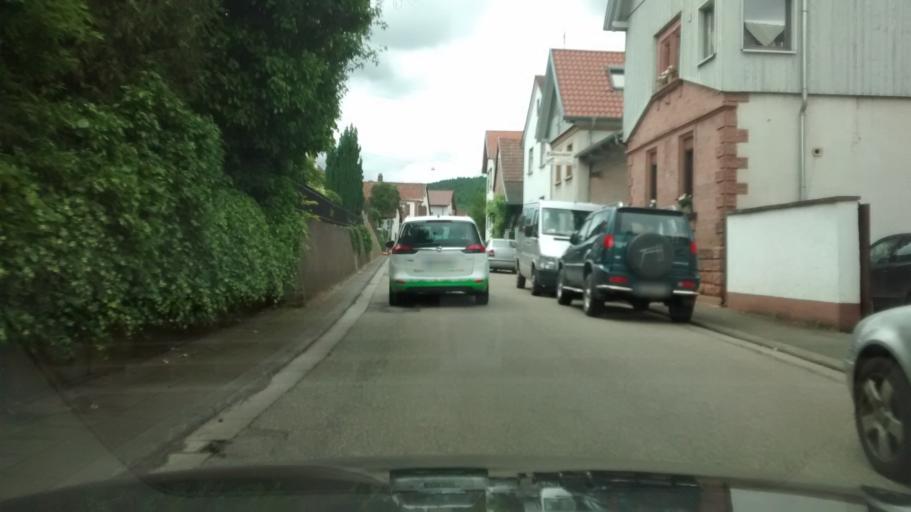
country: DE
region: Rheinland-Pfalz
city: Birkenhordt
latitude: 49.1144
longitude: 7.9348
